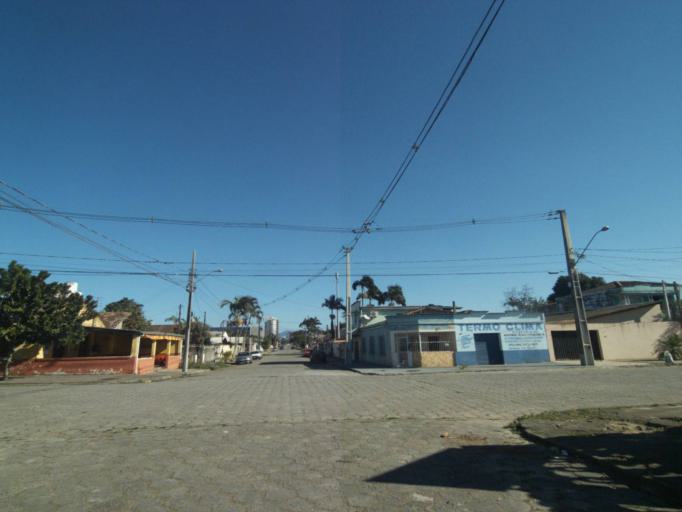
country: BR
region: Parana
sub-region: Paranagua
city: Paranagua
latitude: -25.5112
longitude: -48.5033
